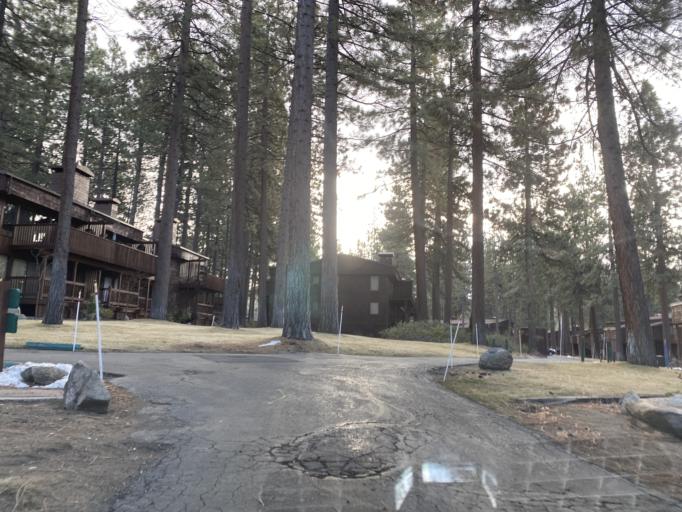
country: US
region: Nevada
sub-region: Douglas County
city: Kingsbury
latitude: 38.9969
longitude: -119.9549
